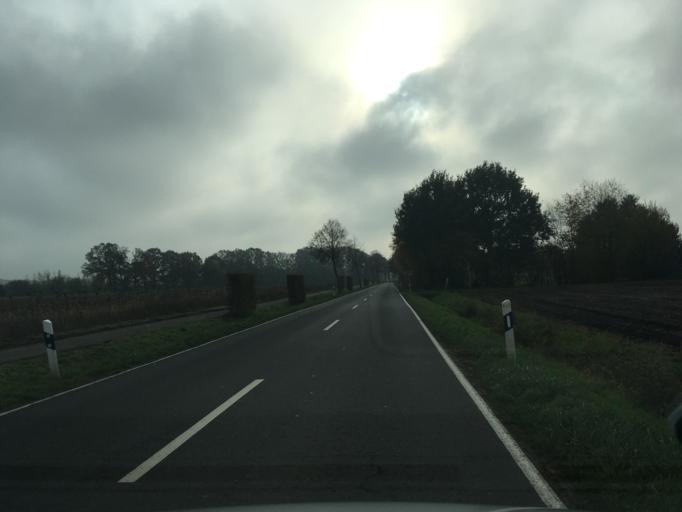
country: DE
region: North Rhine-Westphalia
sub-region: Regierungsbezirk Munster
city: Sudlohn
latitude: 51.9064
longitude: 6.9172
